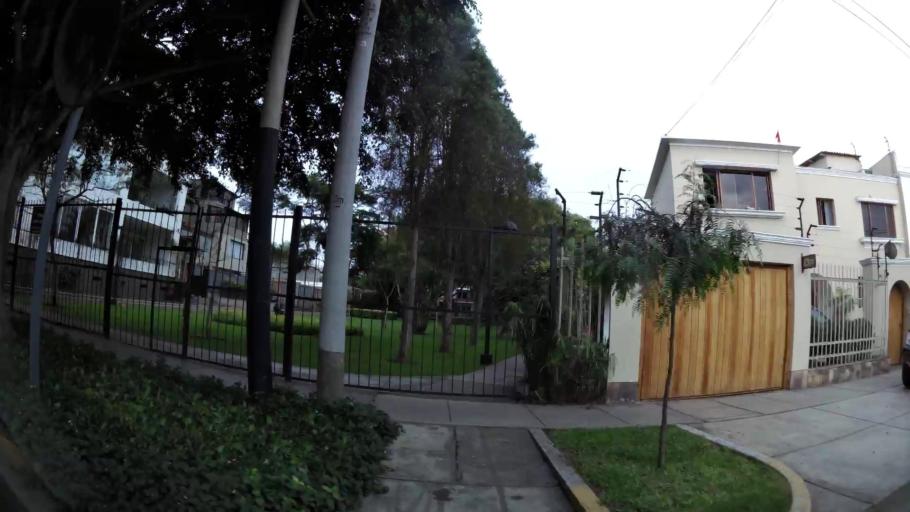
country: PE
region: Lima
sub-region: Lima
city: San Isidro
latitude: -12.1045
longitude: -77.0543
